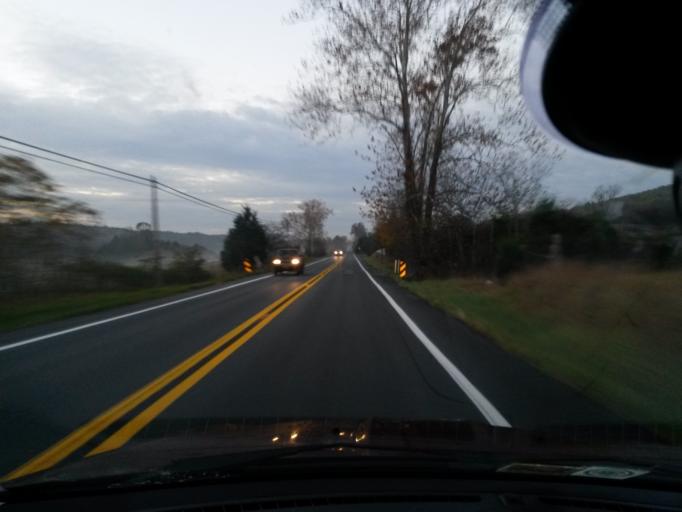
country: US
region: Virginia
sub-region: Alleghany County
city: Clifton Forge
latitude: 37.7305
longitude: -79.8015
